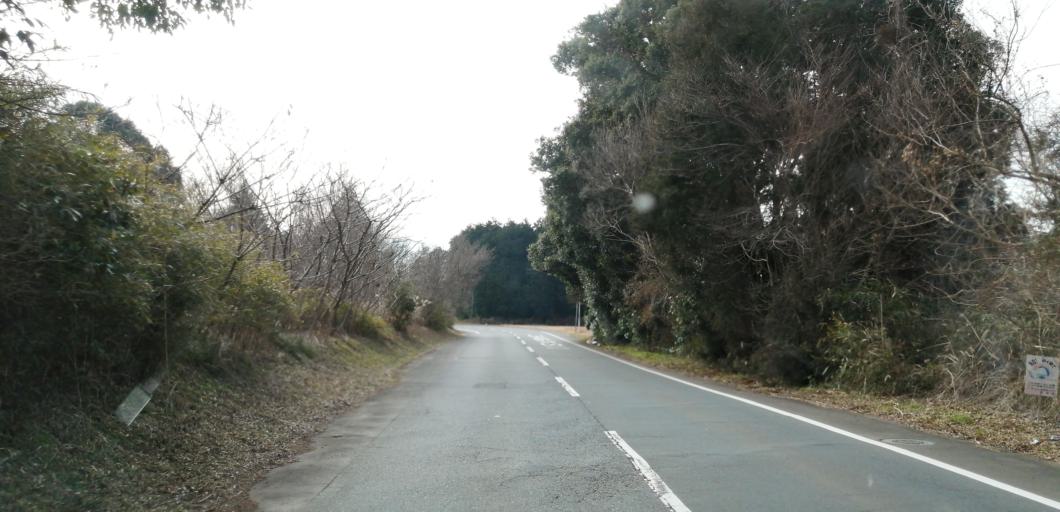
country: JP
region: Chiba
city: Narita
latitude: 35.7690
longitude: 140.3634
